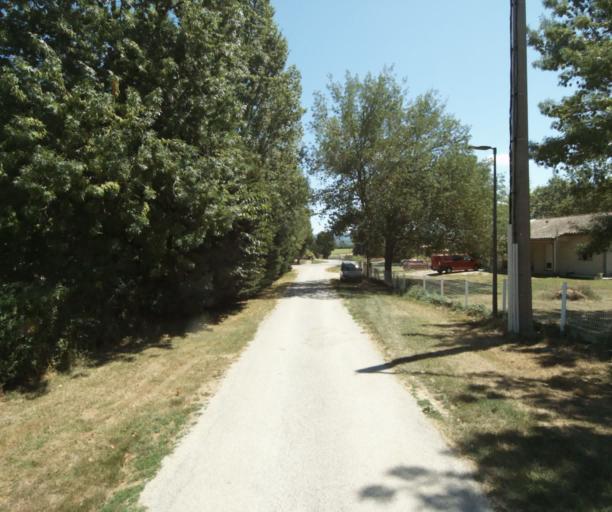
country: FR
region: Midi-Pyrenees
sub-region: Departement de la Haute-Garonne
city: Saint-Felix-Lauragais
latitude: 43.4620
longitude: 1.9278
